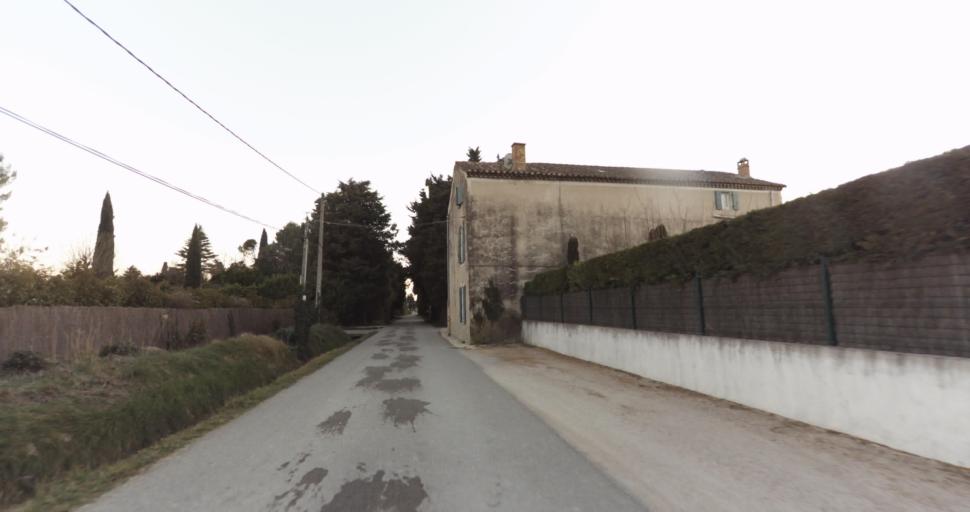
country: FR
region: Provence-Alpes-Cote d'Azur
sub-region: Departement des Bouches-du-Rhone
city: Barbentane
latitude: 43.9100
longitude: 4.7762
